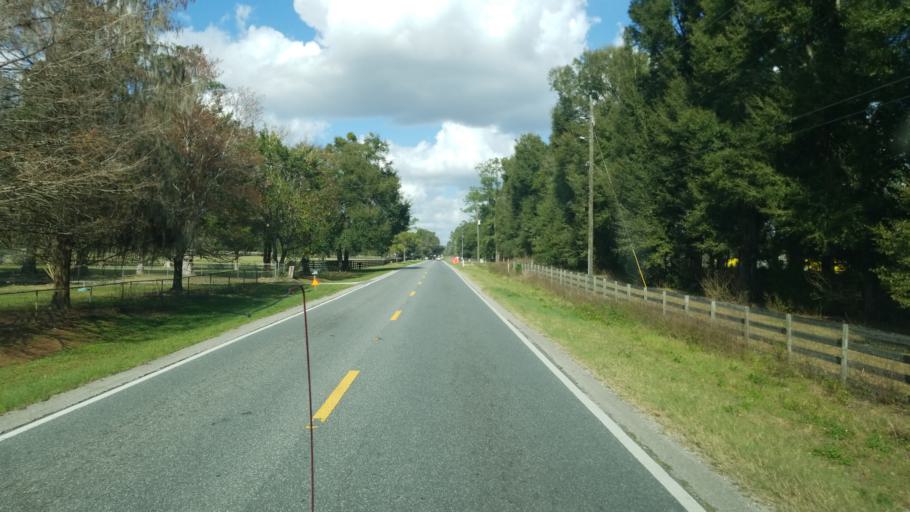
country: US
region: Florida
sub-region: Marion County
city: Belleview
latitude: 28.9967
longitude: -82.1199
